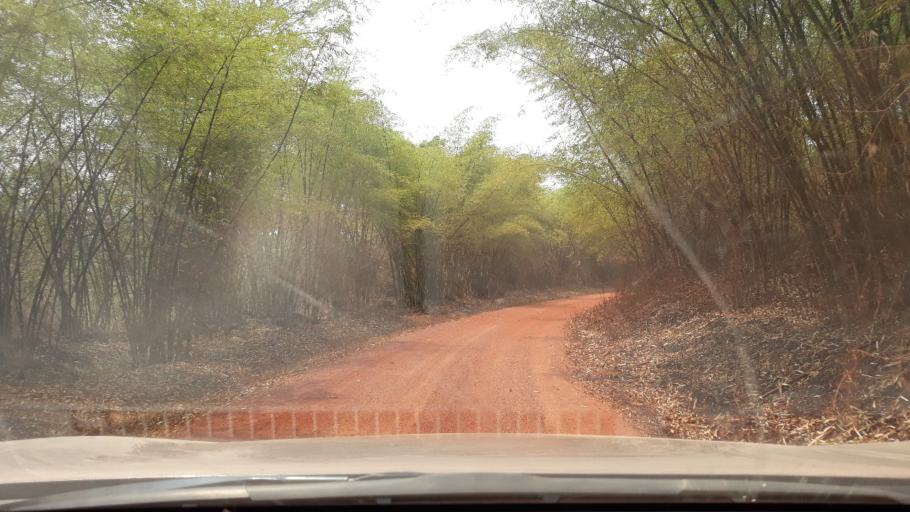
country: CD
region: Eastern Province
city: Buta
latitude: 2.3005
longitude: 25.0228
